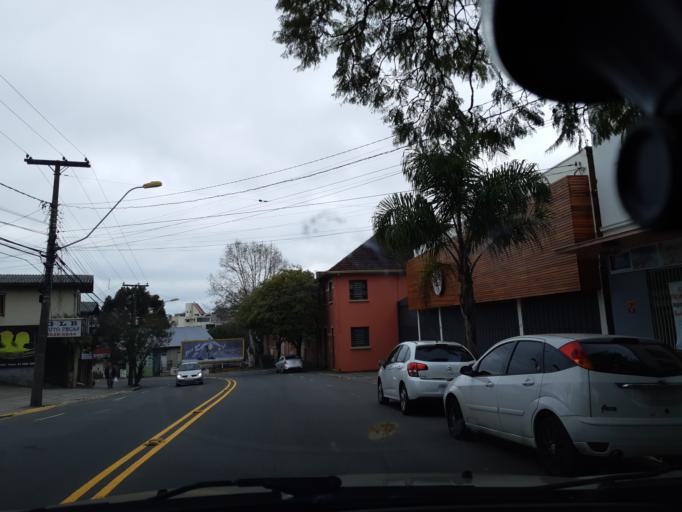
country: BR
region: Rio Grande do Sul
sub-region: Caxias Do Sul
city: Caxias do Sul
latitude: -29.1635
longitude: -51.1886
